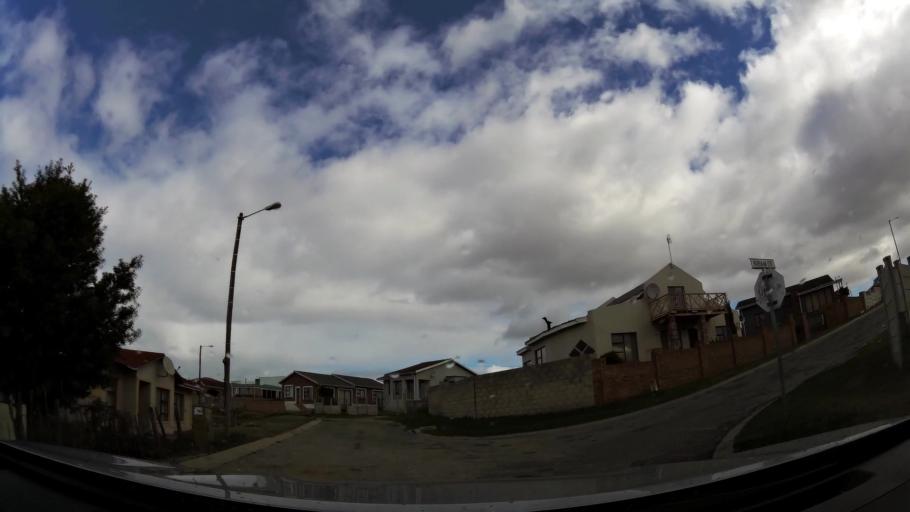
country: ZA
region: Western Cape
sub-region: Eden District Municipality
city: George
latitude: -34.0217
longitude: 22.4769
